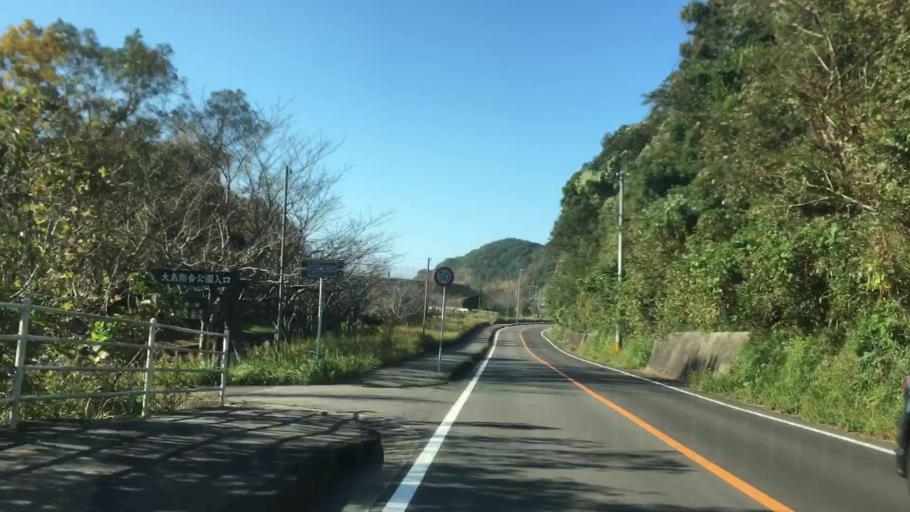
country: JP
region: Nagasaki
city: Sasebo
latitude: 33.0327
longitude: 129.6057
